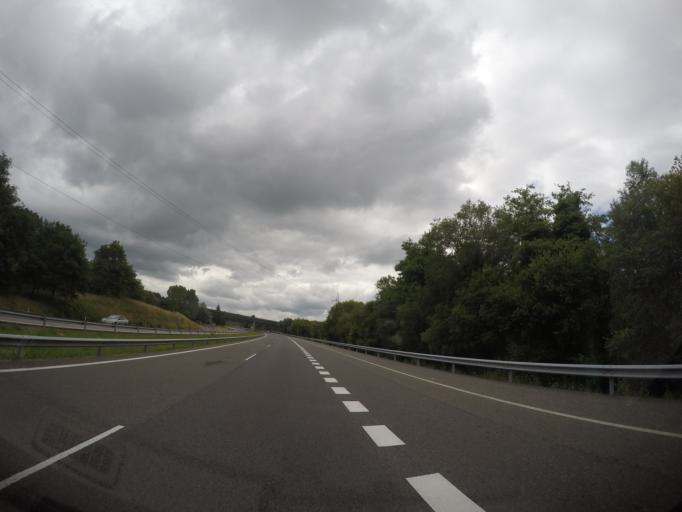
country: ES
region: Galicia
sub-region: Provincia da Coruna
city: Betanzos
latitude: 43.2639
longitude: -8.2539
